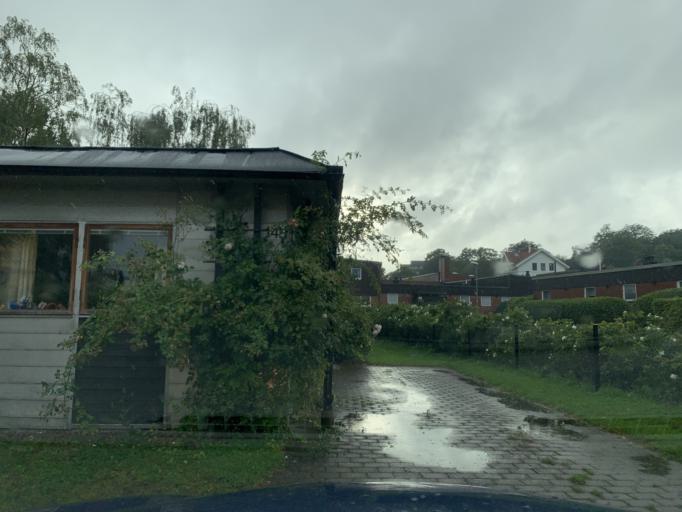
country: SE
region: Vaestra Goetaland
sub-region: Goteborg
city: Goeteborg
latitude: 57.7043
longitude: 12.0123
